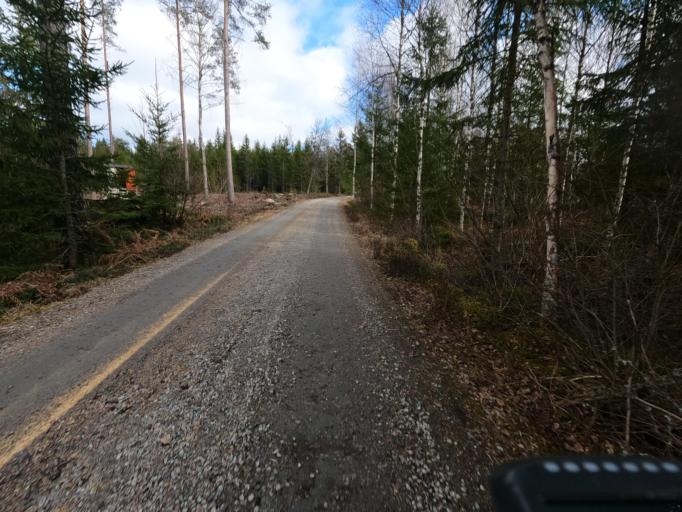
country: SE
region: Kronoberg
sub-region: Alvesta Kommun
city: Vislanda
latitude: 56.8152
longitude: 14.3791
